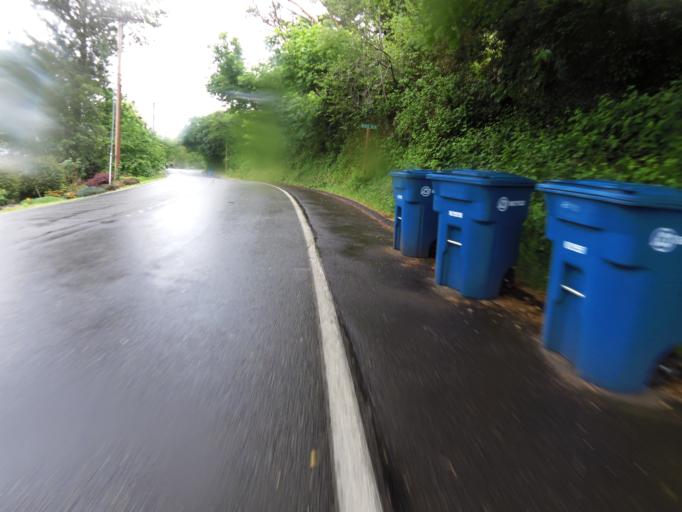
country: US
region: Washington
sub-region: King County
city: Bryn Mawr-Skyway
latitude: 47.5298
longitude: -122.2335
